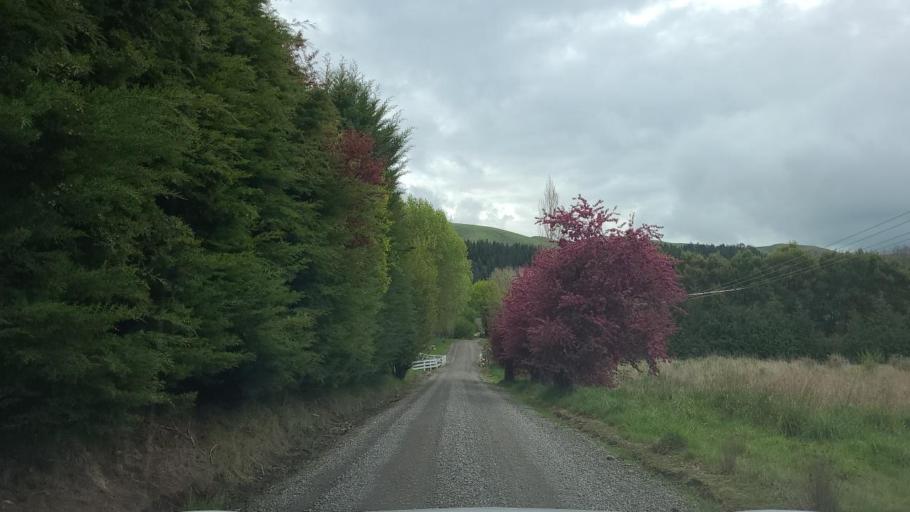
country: NZ
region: Wellington
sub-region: Masterton District
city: Masterton
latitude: -41.1707
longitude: 175.5923
